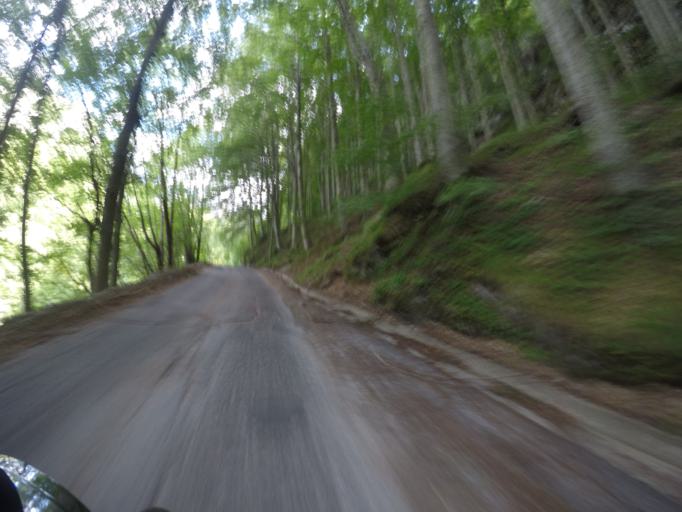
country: IT
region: Tuscany
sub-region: Provincia di Lucca
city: Minucciano
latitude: 44.1444
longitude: 10.1928
